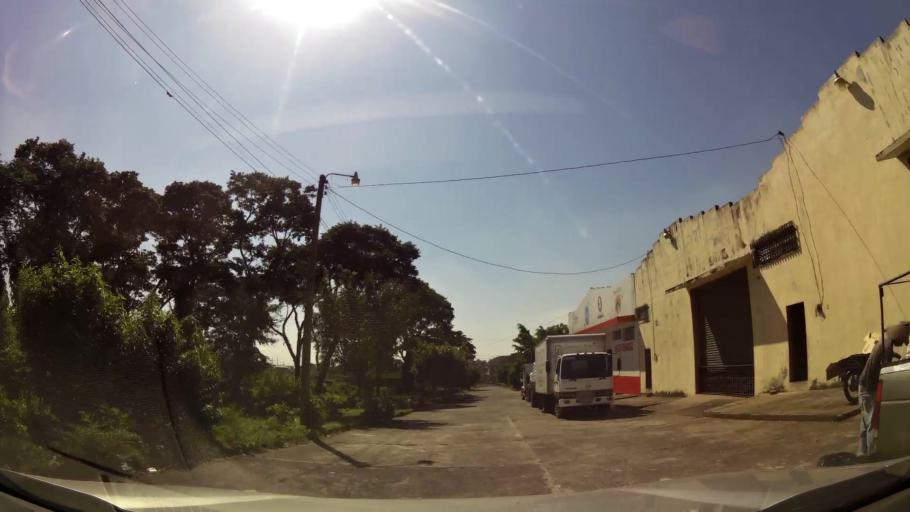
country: GT
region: Suchitepeque
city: Mazatenango
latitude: 14.5476
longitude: -91.5053
